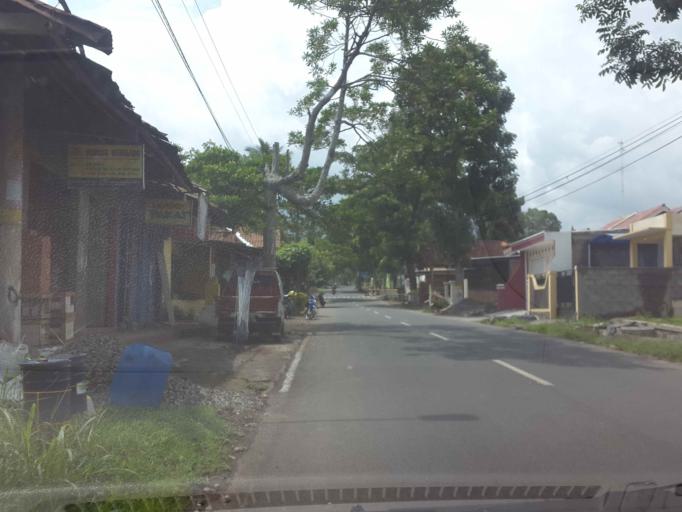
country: ID
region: Central Java
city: Salatiga
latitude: -7.3548
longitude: 110.5060
